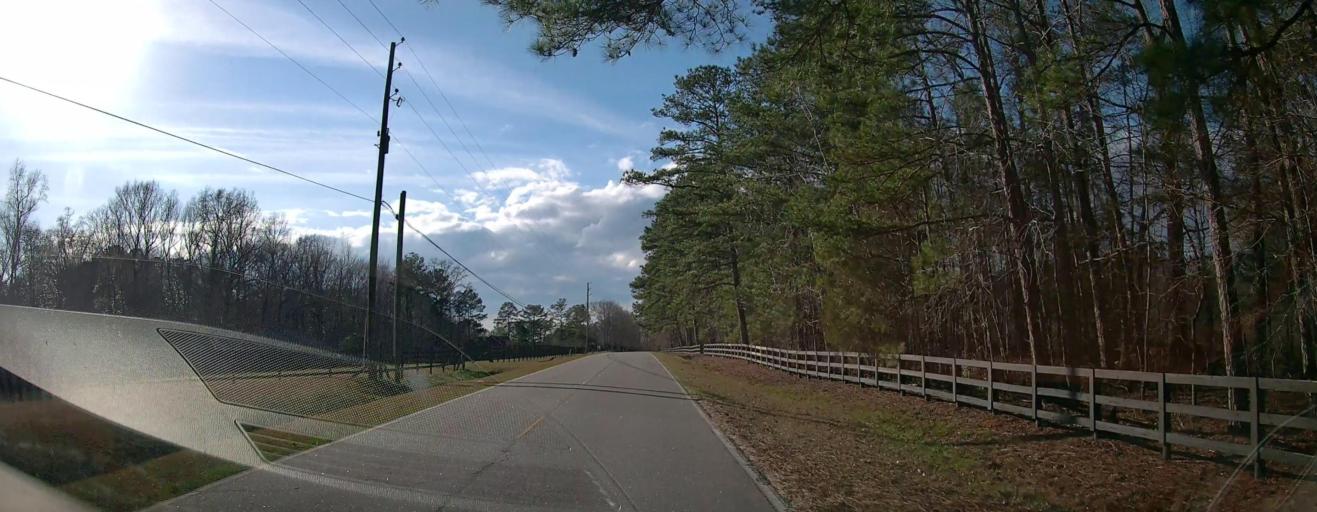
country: US
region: Georgia
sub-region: Harris County
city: Hamilton
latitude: 32.5651
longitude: -84.7965
